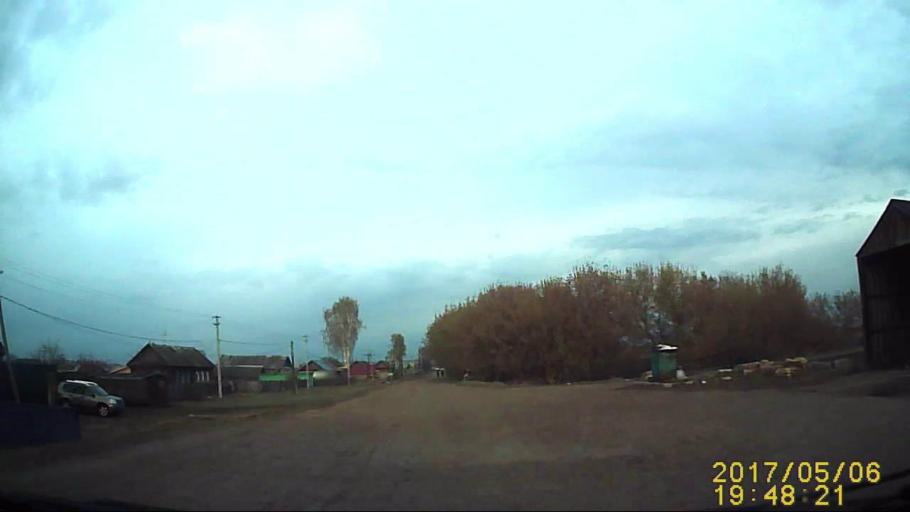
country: RU
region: Ulyanovsk
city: Staraya Mayna
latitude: 54.6016
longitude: 48.9217
